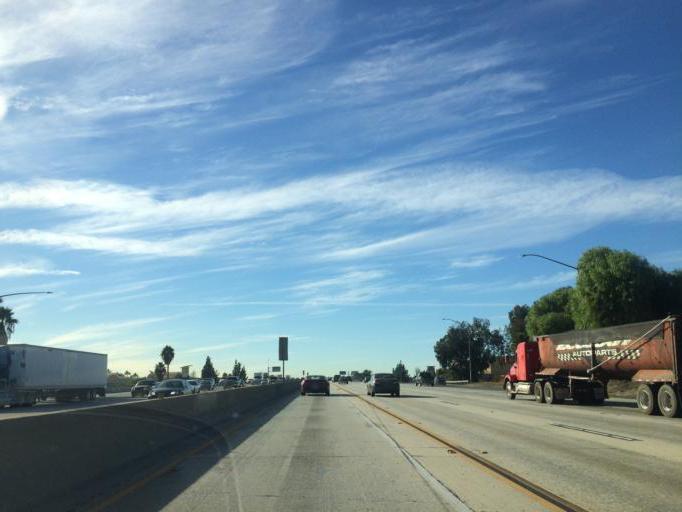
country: US
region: California
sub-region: San Bernardino County
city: Upland
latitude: 34.0874
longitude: -117.6654
